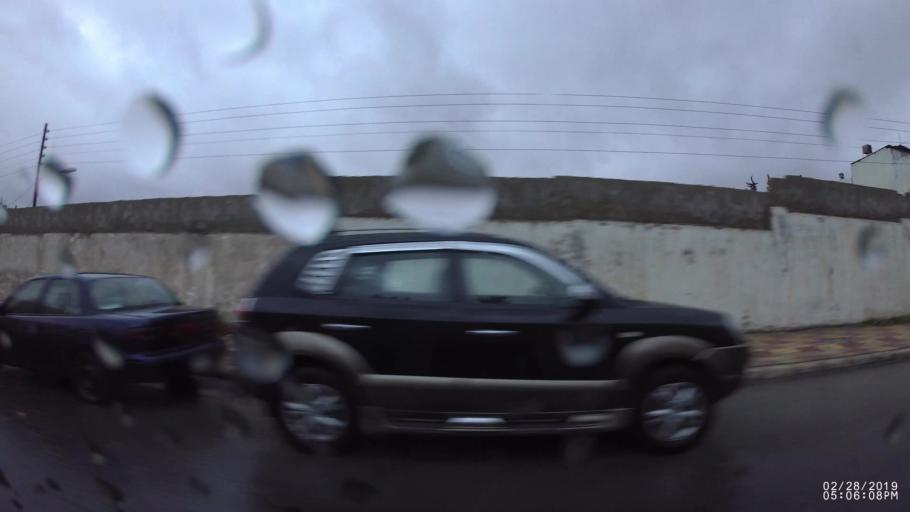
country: JO
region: Amman
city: Amman
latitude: 31.9959
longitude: 35.9286
